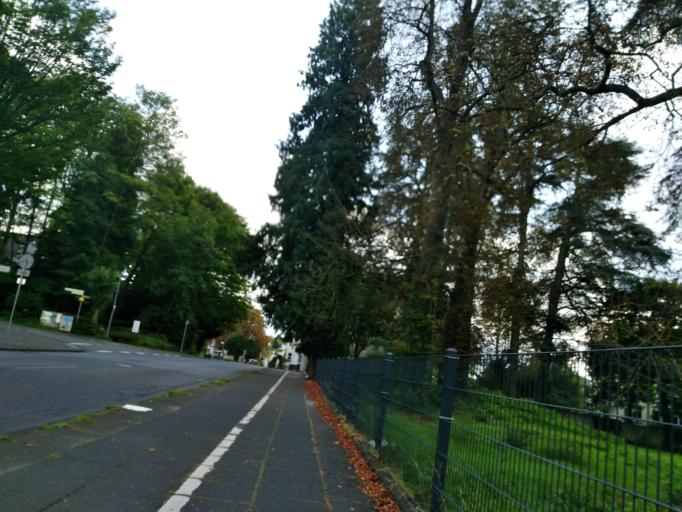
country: DE
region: North Rhine-Westphalia
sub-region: Regierungsbezirk Koln
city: Bad Honnef
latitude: 50.6501
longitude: 7.2200
